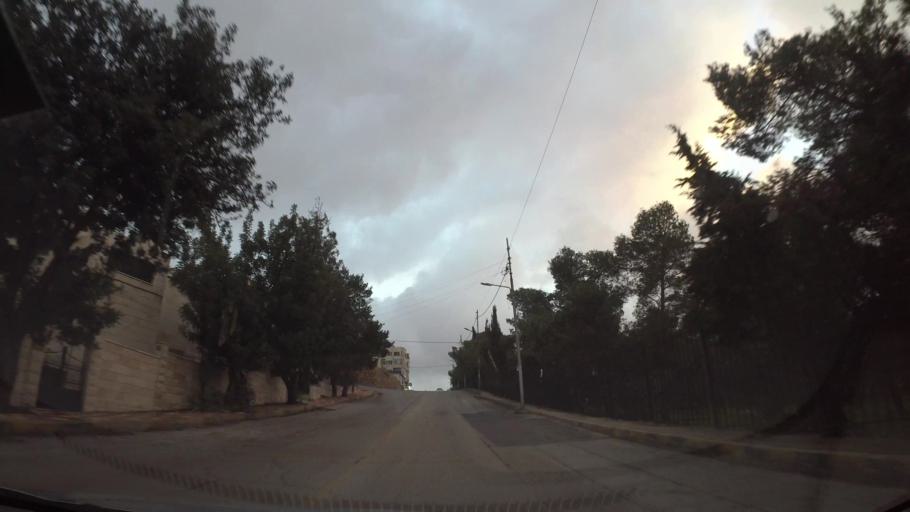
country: JO
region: Amman
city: Al Jubayhah
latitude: 32.0111
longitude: 35.8780
